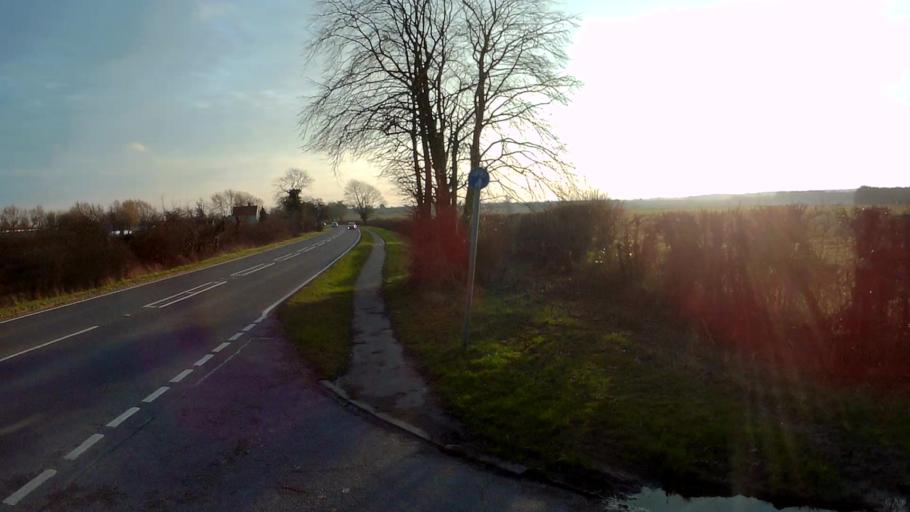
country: GB
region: England
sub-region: Lincolnshire
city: Bourne
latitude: 52.7853
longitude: -0.3772
